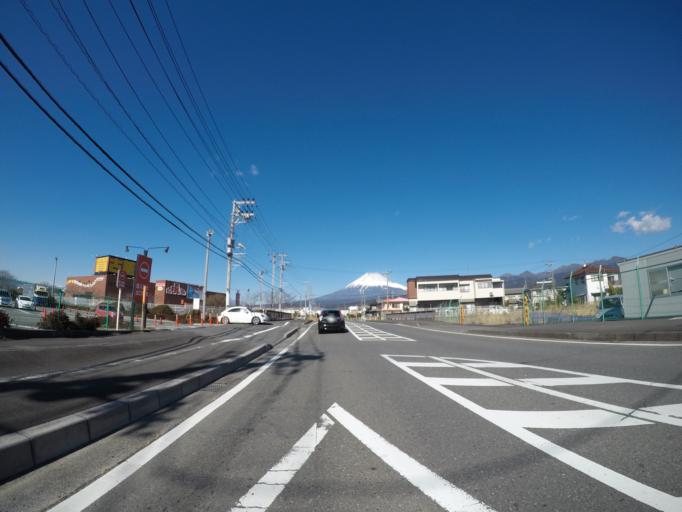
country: JP
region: Shizuoka
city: Fuji
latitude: 35.1401
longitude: 138.7413
